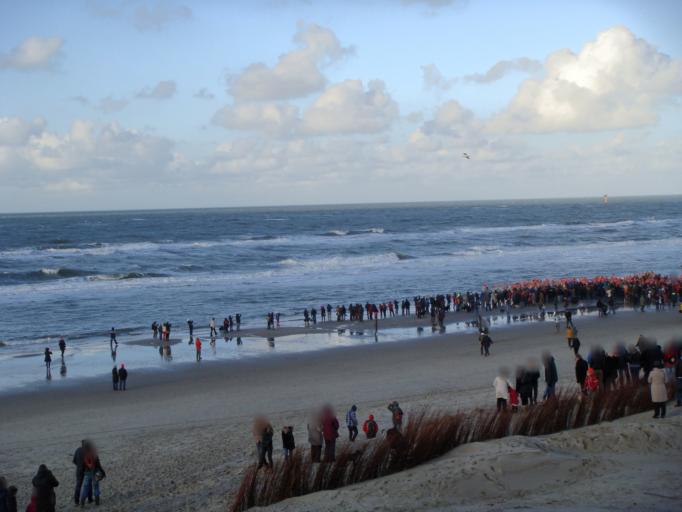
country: NL
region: North Holland
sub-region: Gemeente Texel
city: Den Burg
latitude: 53.1015
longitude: 4.7556
